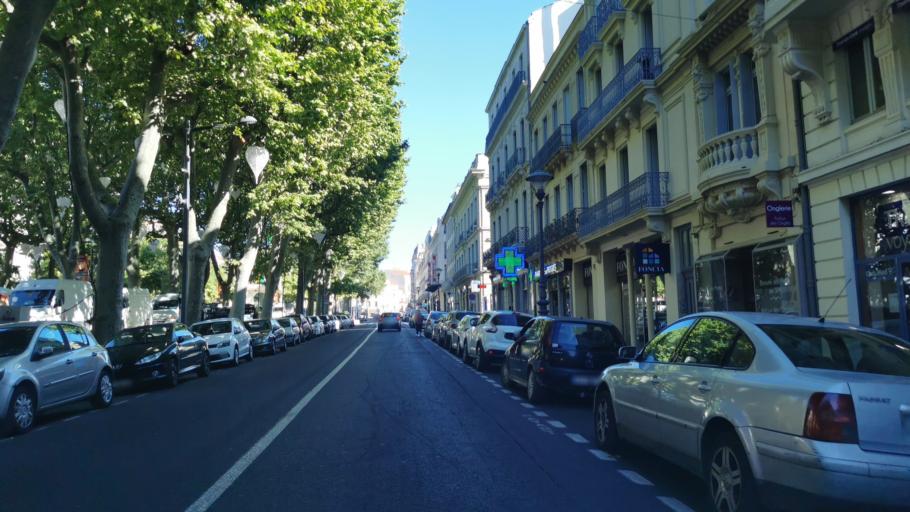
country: FR
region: Languedoc-Roussillon
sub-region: Departement de l'Herault
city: Beziers
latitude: 43.3429
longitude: 3.2170
